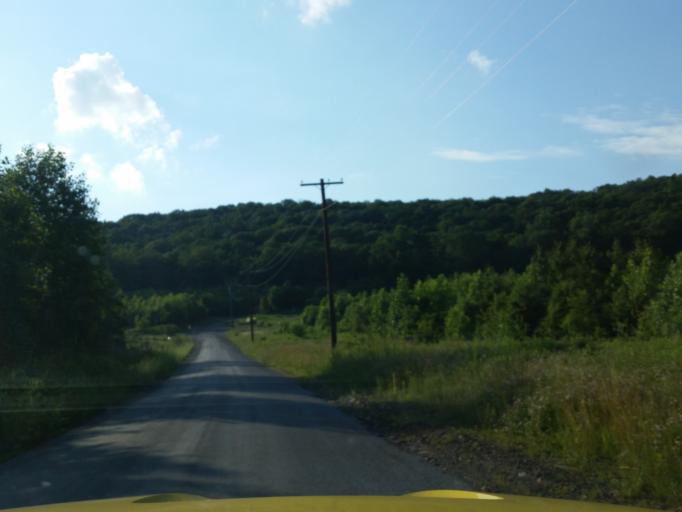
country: US
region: Pennsylvania
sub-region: Dauphin County
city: Williamstown
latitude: 40.4613
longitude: -76.6270
